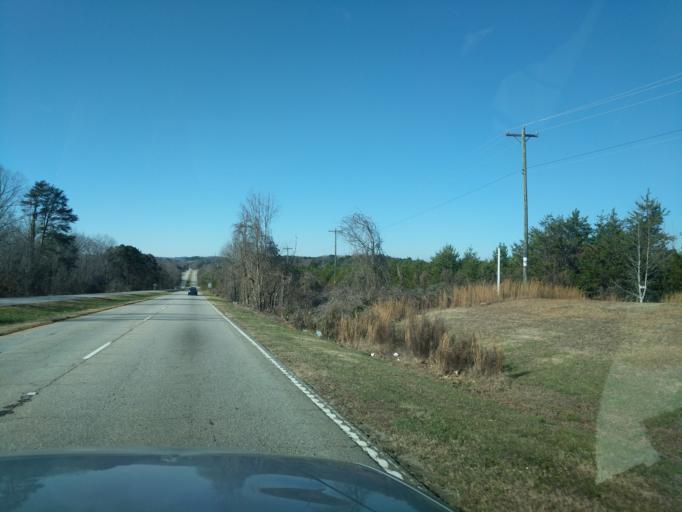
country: US
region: South Carolina
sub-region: Greenville County
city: Parker
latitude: 34.8337
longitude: -82.4616
